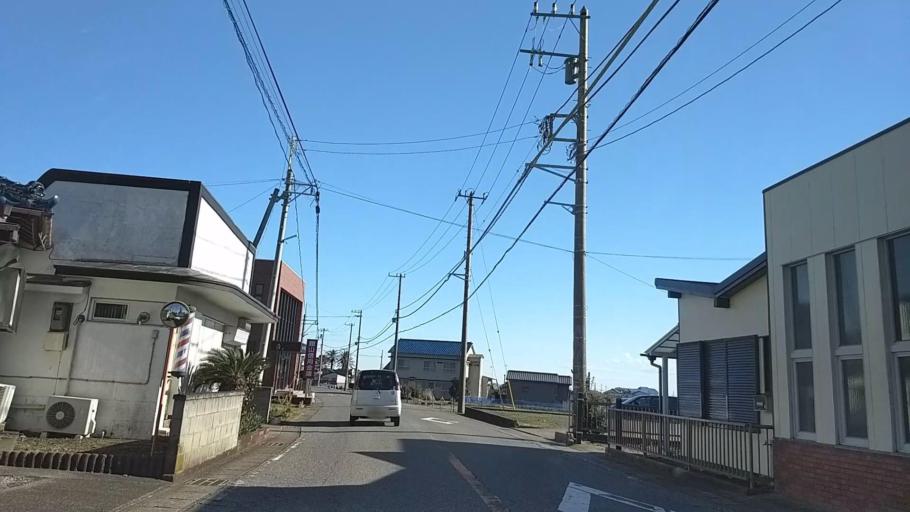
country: JP
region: Chiba
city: Tateyama
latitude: 34.9075
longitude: 139.9009
